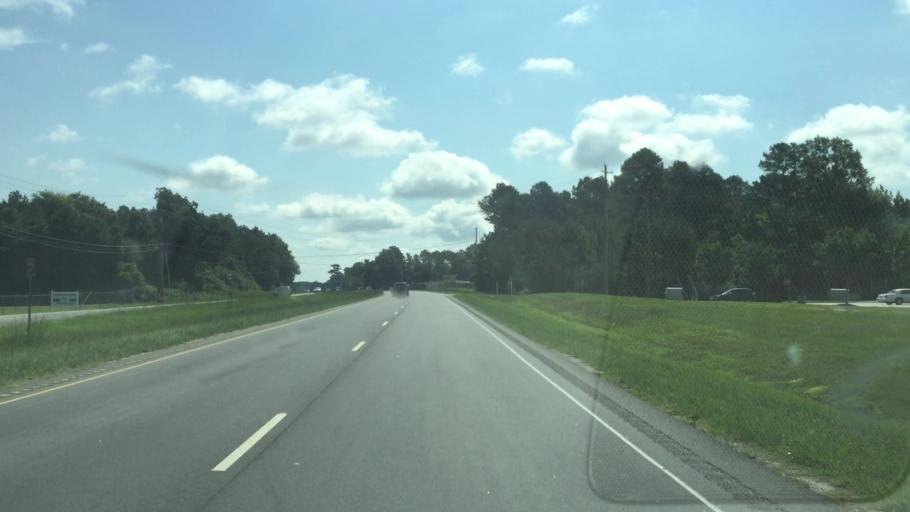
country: US
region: North Carolina
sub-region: Anson County
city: Wadesboro
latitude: 34.9785
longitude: -80.1104
